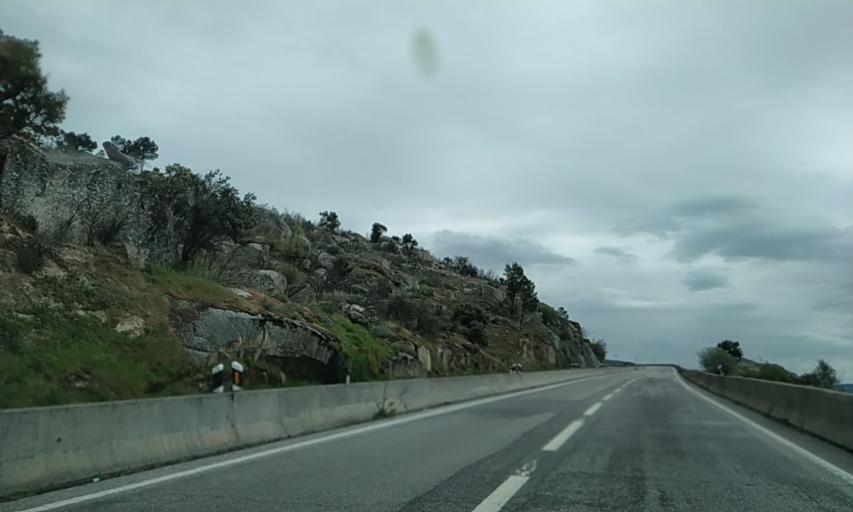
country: PT
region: Guarda
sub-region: Guarda
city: Guarda
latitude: 40.6071
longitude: -7.2829
